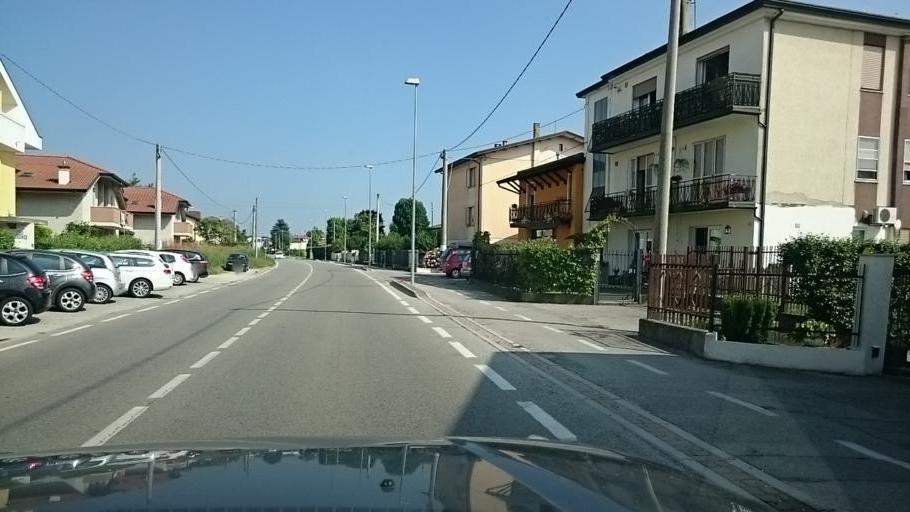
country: IT
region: Veneto
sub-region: Provincia di Padova
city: Saletto
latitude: 45.4636
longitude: 11.8714
